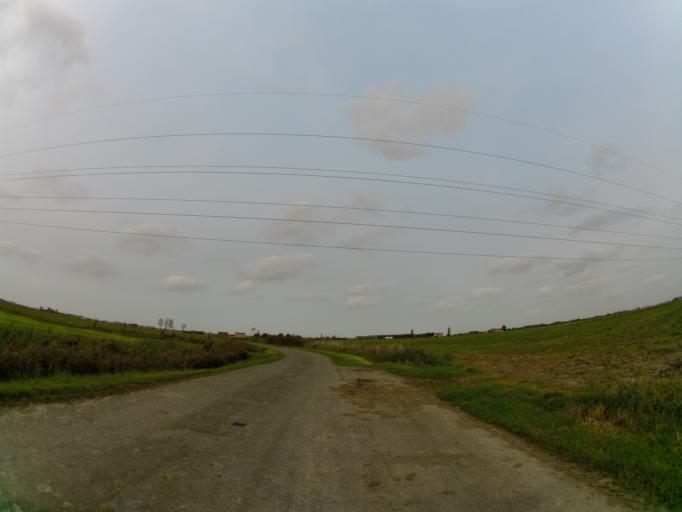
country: BE
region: Flanders
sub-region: Provincie West-Vlaanderen
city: Oudenburg
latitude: 51.2239
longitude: 3.0235
